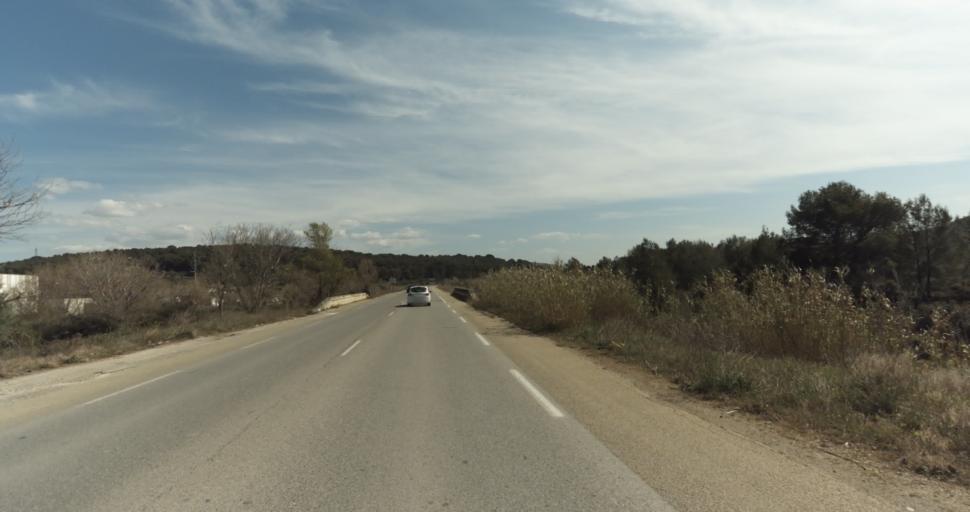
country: FR
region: Provence-Alpes-Cote d'Azur
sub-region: Departement des Bouches-du-Rhone
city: Coudoux
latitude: 43.5465
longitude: 5.2528
